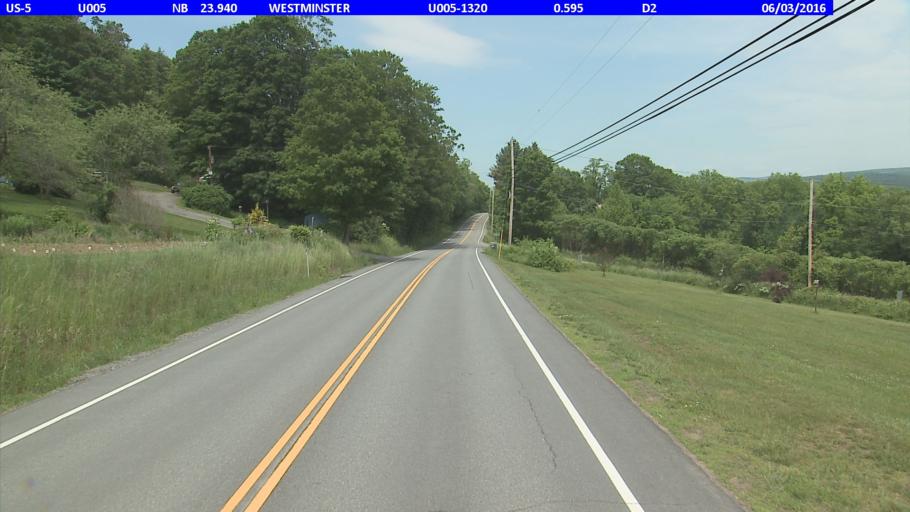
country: US
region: New Hampshire
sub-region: Cheshire County
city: Westmoreland
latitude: 43.0289
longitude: -72.4680
